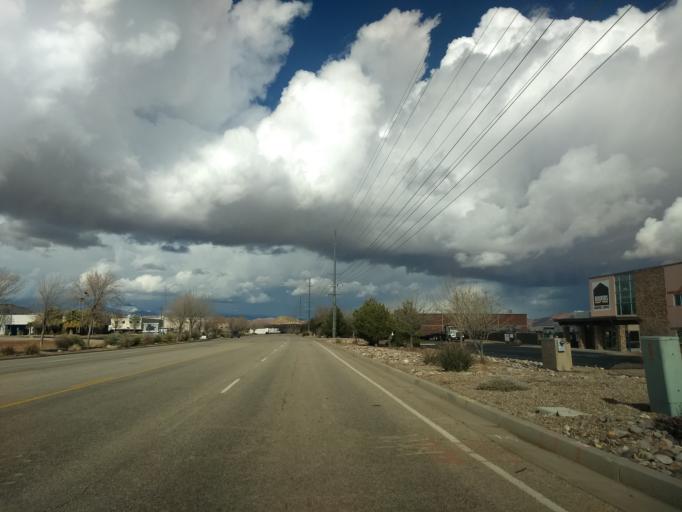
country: US
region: Utah
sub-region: Washington County
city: Saint George
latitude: 37.0345
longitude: -113.5607
